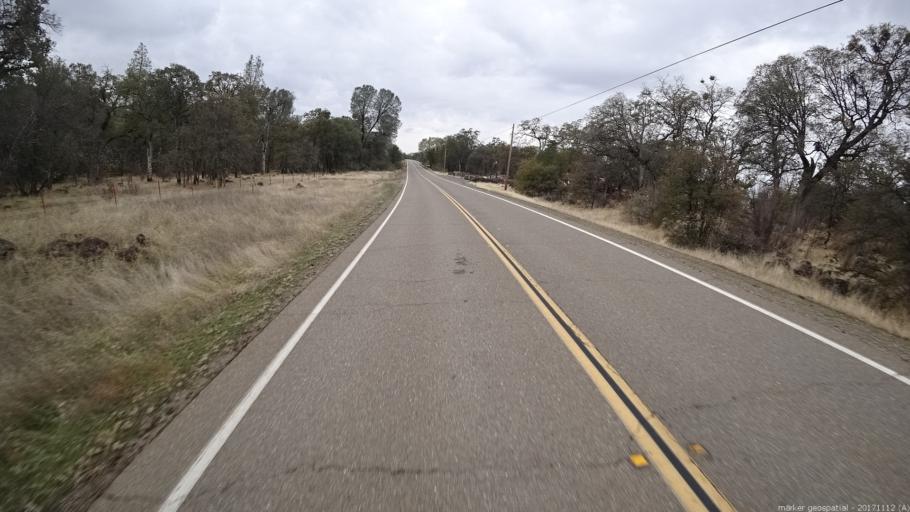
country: US
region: California
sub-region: Shasta County
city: Shingletown
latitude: 40.4887
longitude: -122.0712
